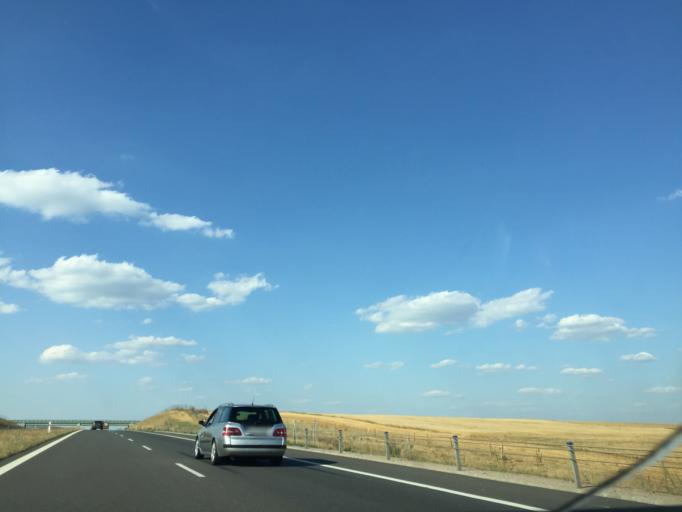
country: PL
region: Swietokrzyskie
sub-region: Powiat jedrzejowski
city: Sobkow
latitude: 50.7133
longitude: 20.4073
